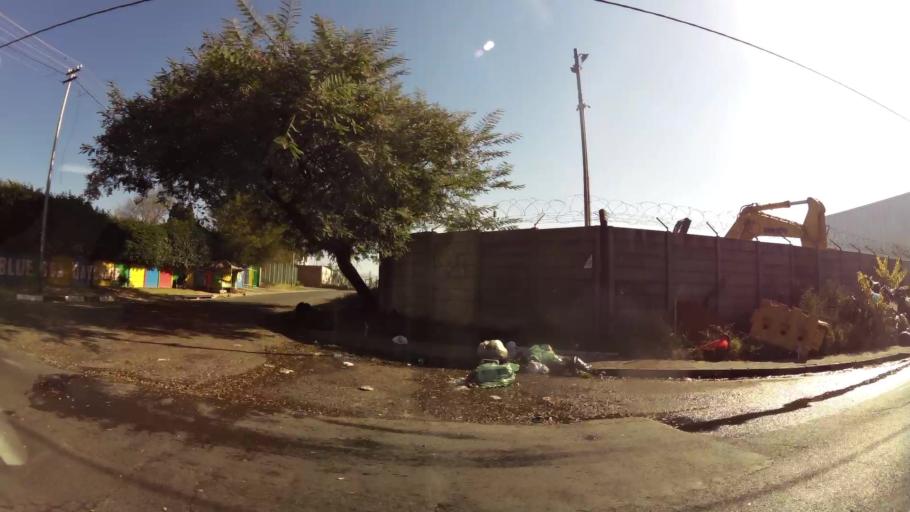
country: ZA
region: Gauteng
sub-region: City of Johannesburg Metropolitan Municipality
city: Modderfontein
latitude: -26.1195
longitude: 28.0955
